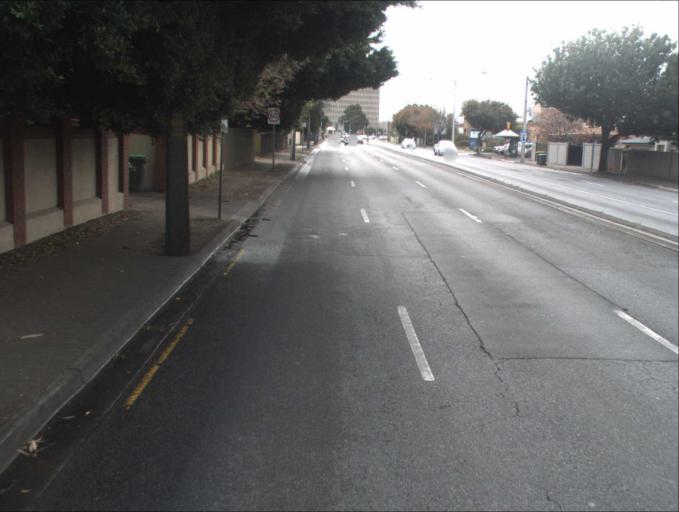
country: AU
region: South Australia
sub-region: Prospect
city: Prospect
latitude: -34.8925
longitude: 138.6101
